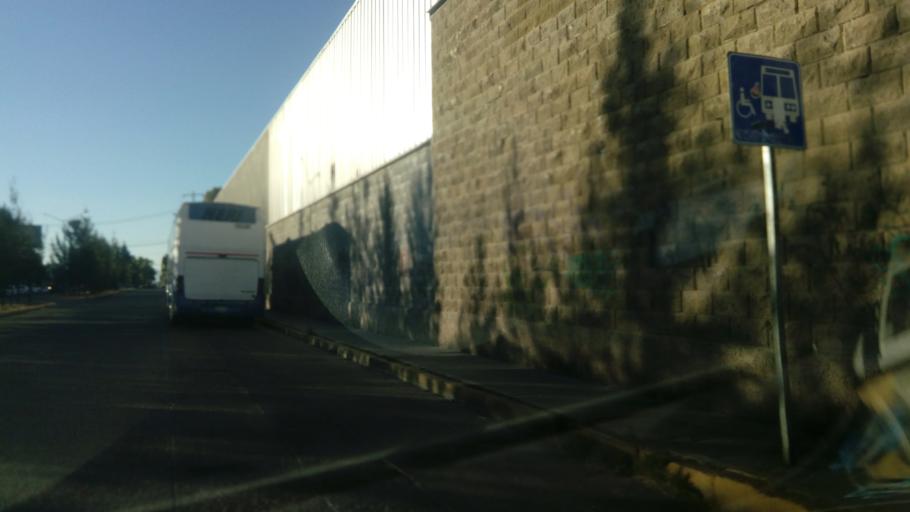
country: MX
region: Durango
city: Victoria de Durango
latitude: 24.0668
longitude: -104.6007
